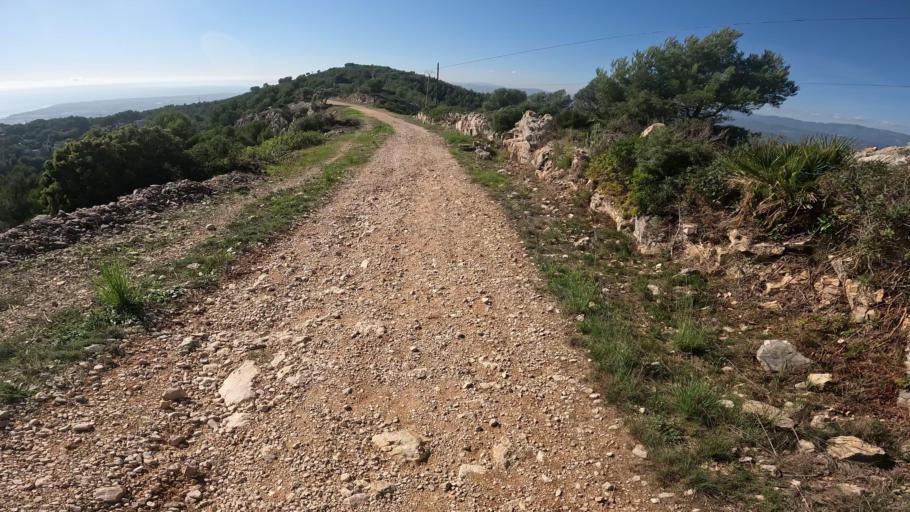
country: ES
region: Valencia
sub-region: Provincia de Castello
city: Alcoceber
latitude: 40.2695
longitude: 0.2741
